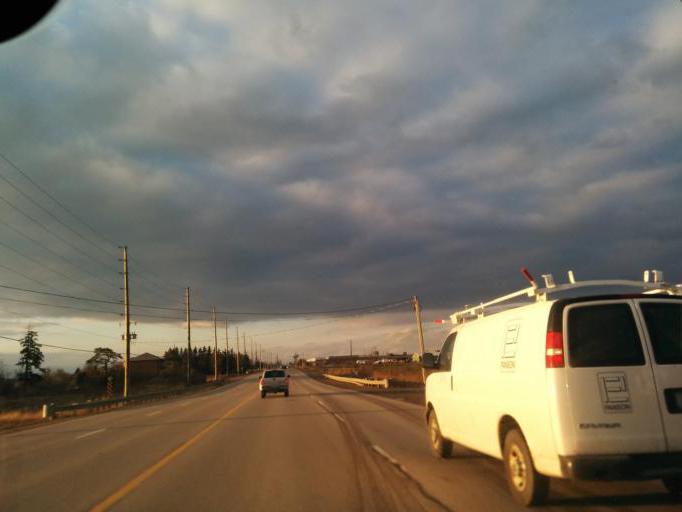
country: CA
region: Ontario
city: Brampton
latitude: 43.8524
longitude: -79.7243
